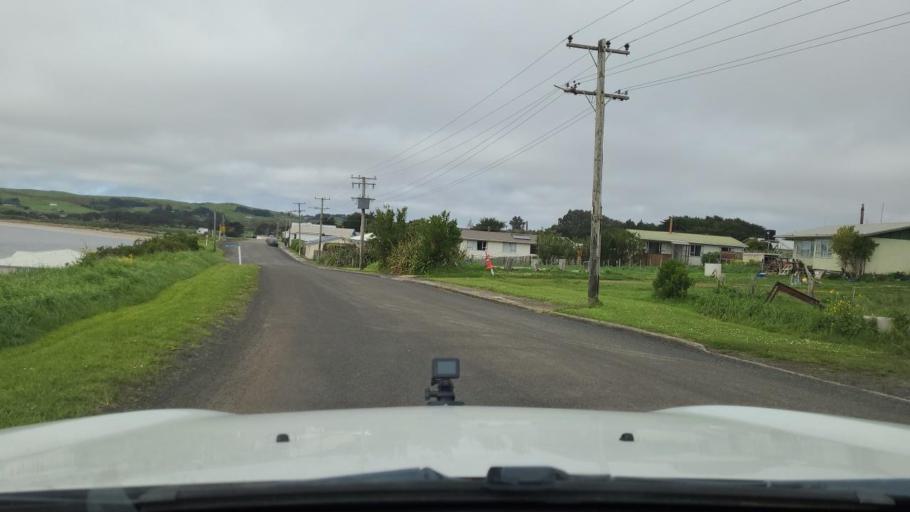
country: NZ
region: Chatham Islands
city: Waitangi
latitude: -43.9505
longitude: -176.5622
